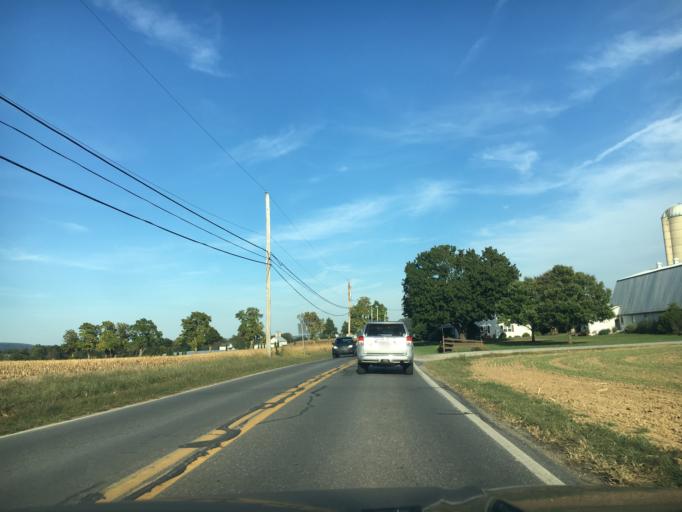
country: US
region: Pennsylvania
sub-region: Lancaster County
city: Brownstown
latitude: 40.1261
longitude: -76.1882
